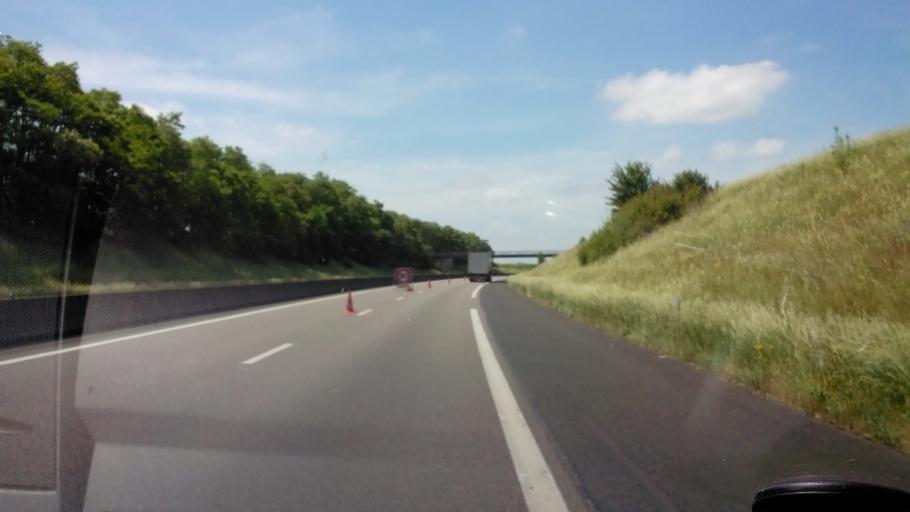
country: FR
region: Lorraine
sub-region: Departement des Vosges
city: Bulgneville
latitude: 48.2317
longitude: 5.8603
